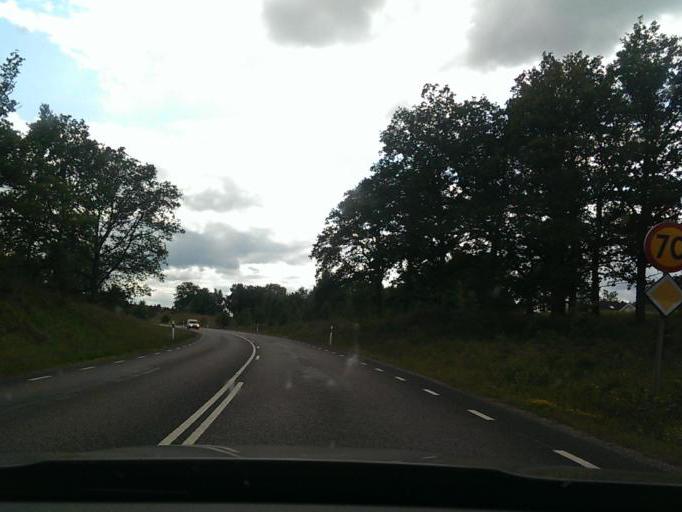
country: SE
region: Joenkoeping
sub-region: Varnamo Kommun
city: Varnamo
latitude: 57.1964
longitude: 14.0170
